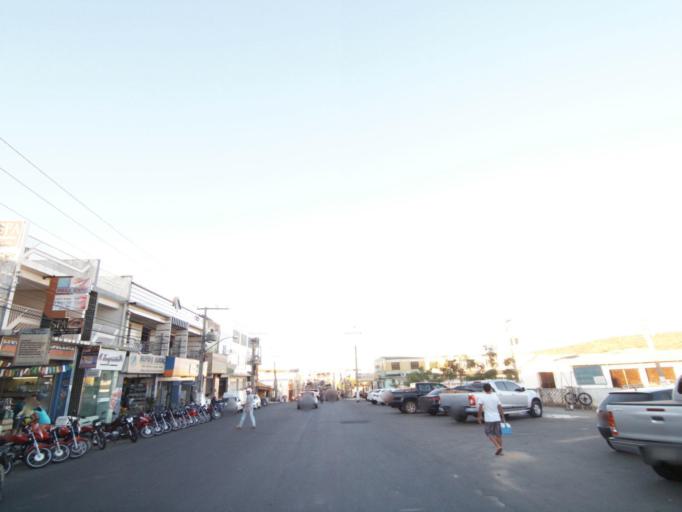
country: BR
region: Bahia
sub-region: Brumado
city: Brumado
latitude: -14.2103
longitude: -41.6707
